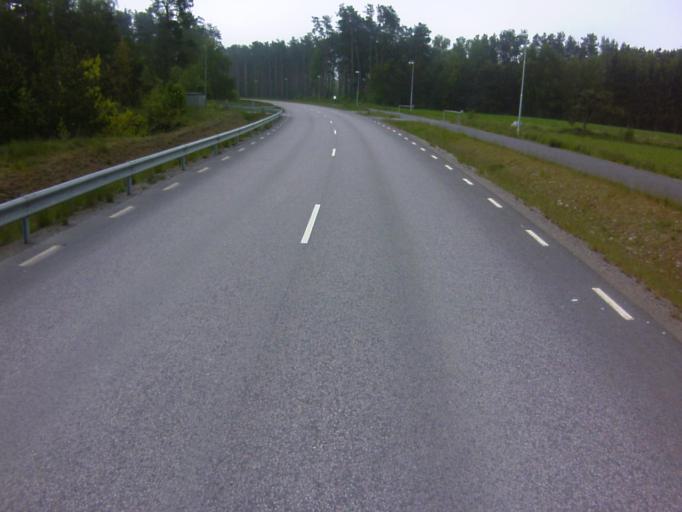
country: SE
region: Blekinge
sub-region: Solvesborgs Kommun
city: Soelvesborg
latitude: 56.0471
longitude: 14.6089
